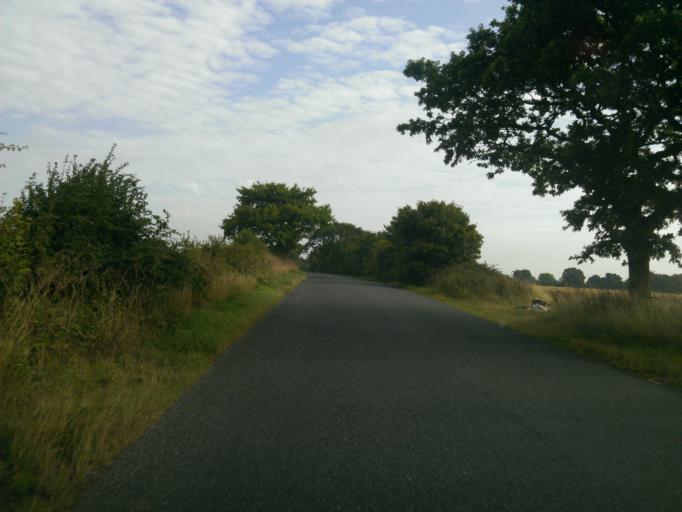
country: GB
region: England
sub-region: Essex
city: Saint Osyth
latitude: 51.8133
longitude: 1.0928
